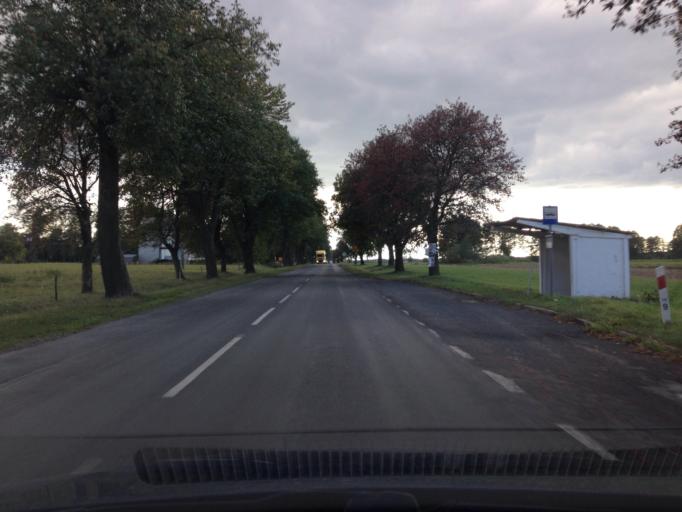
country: PL
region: Kujawsko-Pomorskie
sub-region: Powiat rypinski
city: Rogowo
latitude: 52.9719
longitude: 19.3257
